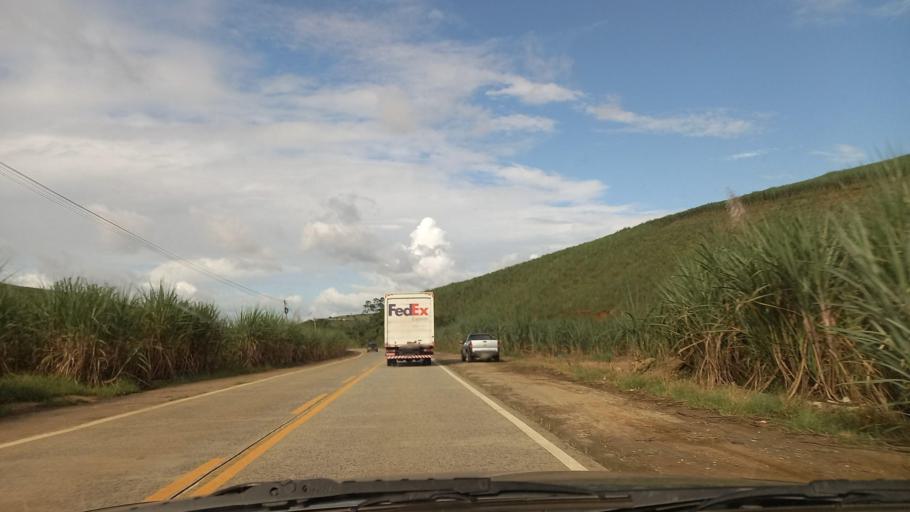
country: BR
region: Pernambuco
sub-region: Palmares
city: Palmares
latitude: -8.6948
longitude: -35.6502
